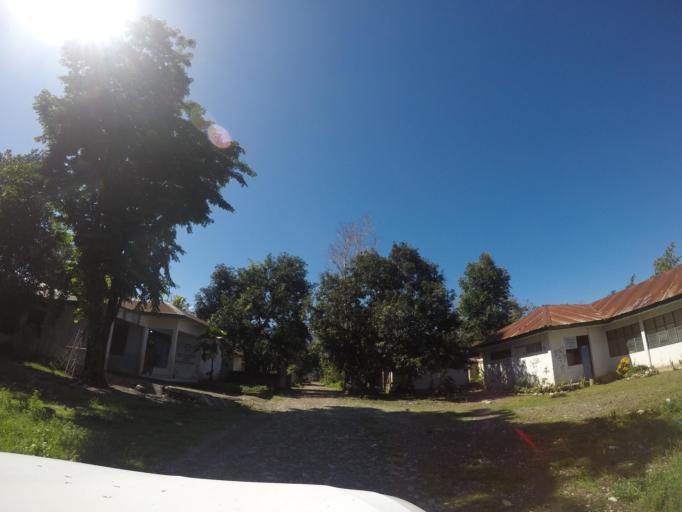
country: TL
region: Bobonaro
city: Maliana
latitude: -8.9892
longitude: 125.2136
